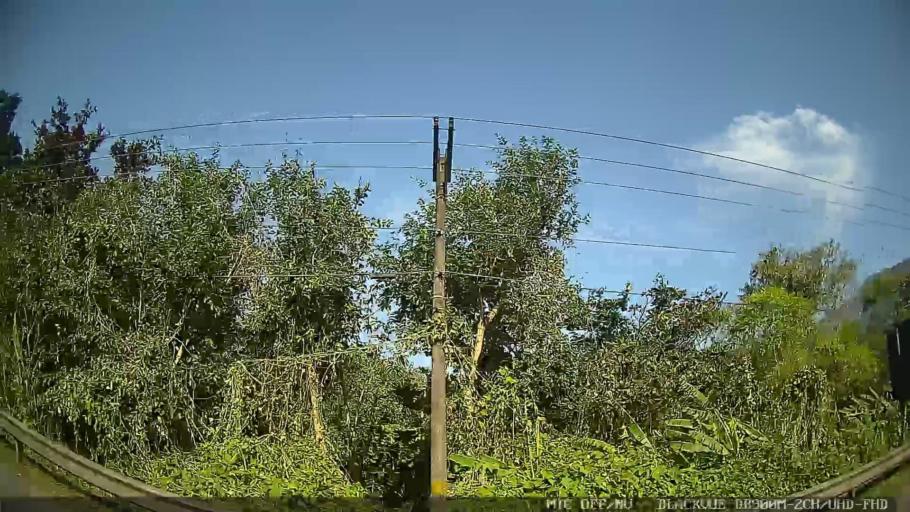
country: BR
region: Sao Paulo
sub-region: Cubatao
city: Cubatao
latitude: -23.8825
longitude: -46.4475
